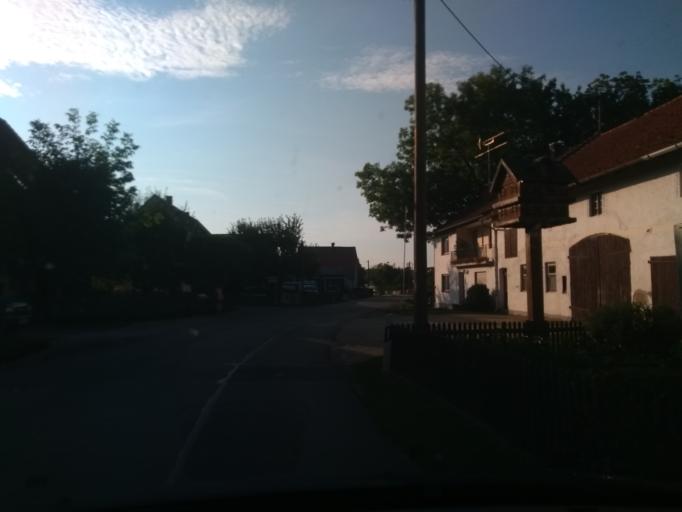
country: DE
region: Bavaria
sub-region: Upper Bavaria
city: Schwabhausen
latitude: 48.3820
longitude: 11.3502
